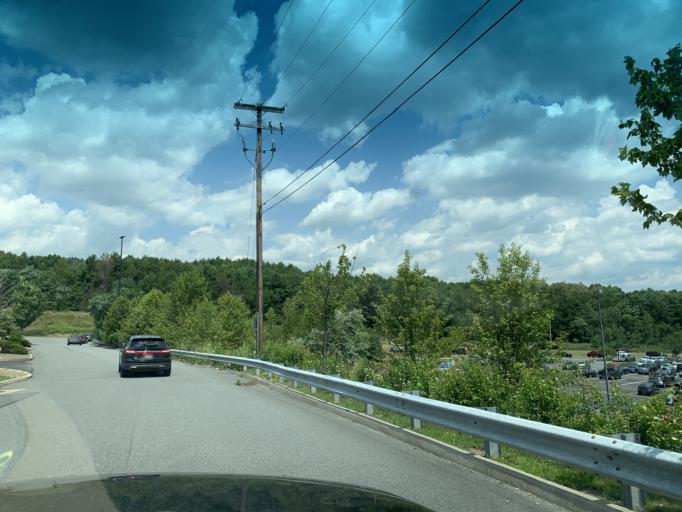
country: US
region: Pennsylvania
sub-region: Lackawanna County
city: Throop
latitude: 41.4533
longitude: -75.6443
